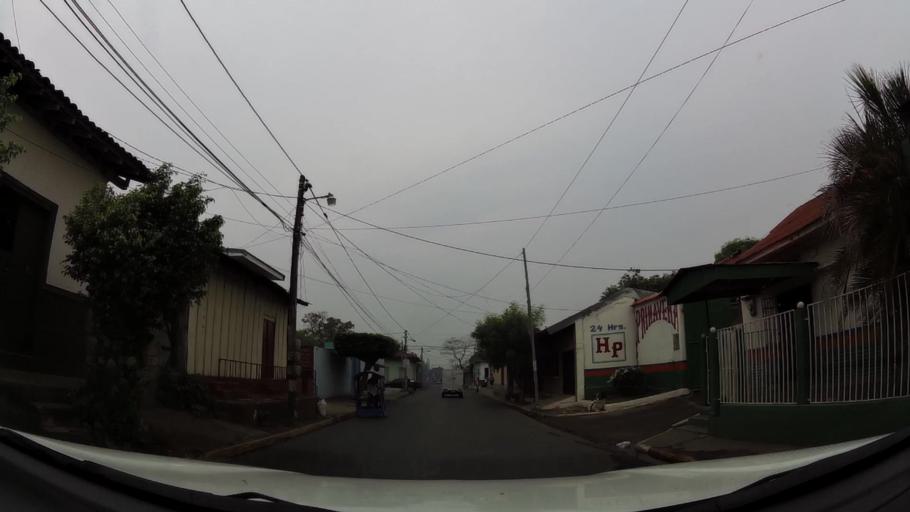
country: NI
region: Leon
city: Leon
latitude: 12.4467
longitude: -86.8754
